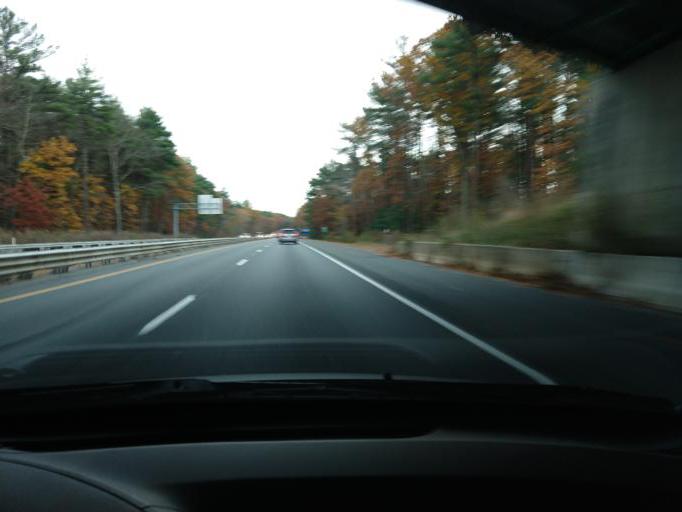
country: US
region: Massachusetts
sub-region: Middlesex County
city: Acton
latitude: 42.4909
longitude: -71.4599
